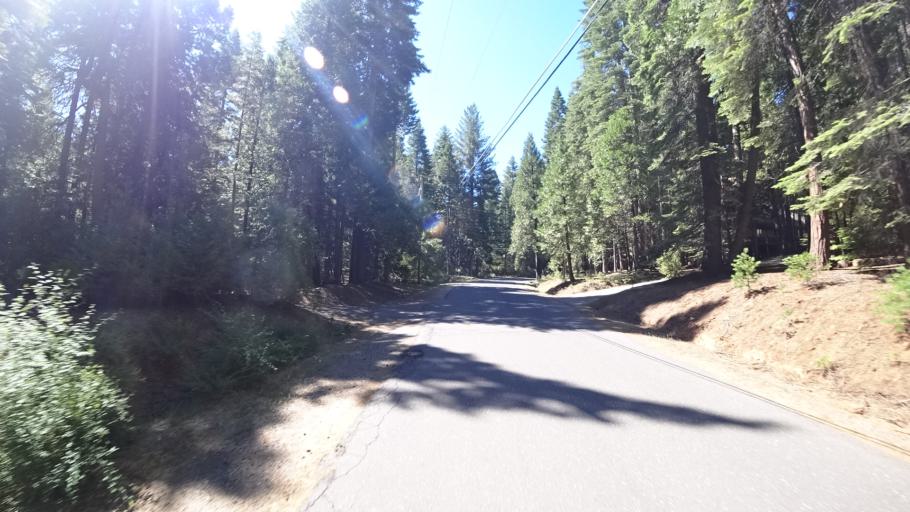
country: US
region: California
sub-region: Calaveras County
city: Arnold
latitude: 38.2839
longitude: -120.2764
